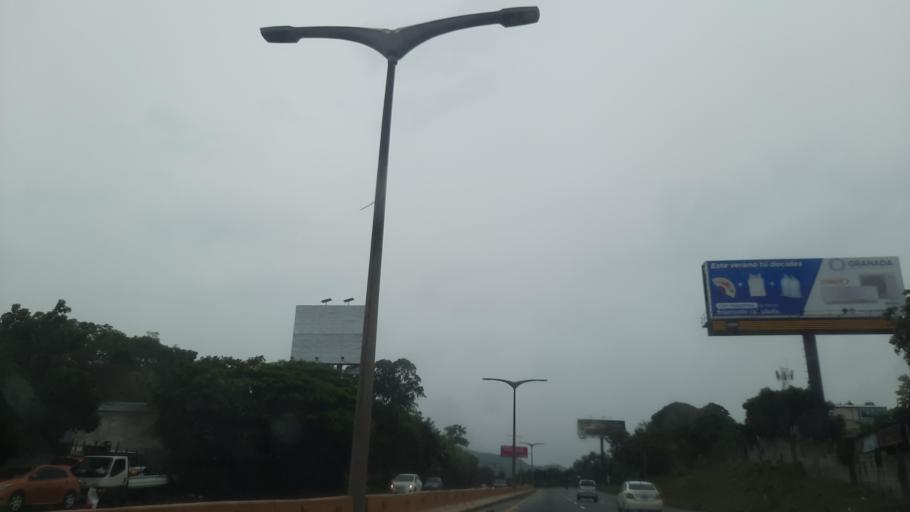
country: SV
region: La Libertad
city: Santa Tecla
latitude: 13.6864
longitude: -89.2923
